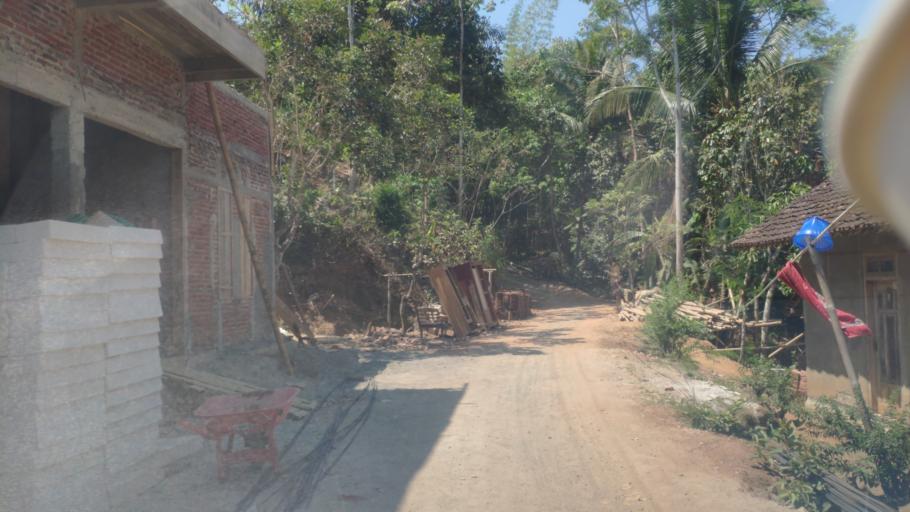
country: ID
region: Central Java
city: Wonosobo
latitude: -7.4252
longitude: 109.6892
